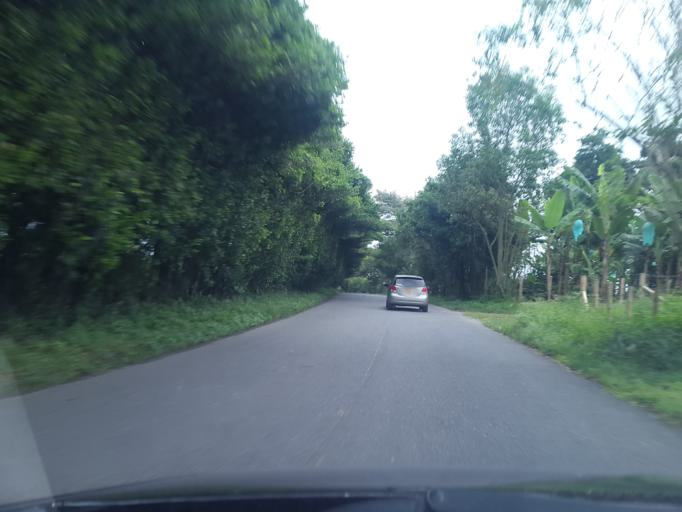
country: CO
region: Quindio
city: La Tebaida
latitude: 4.4964
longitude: -75.7958
